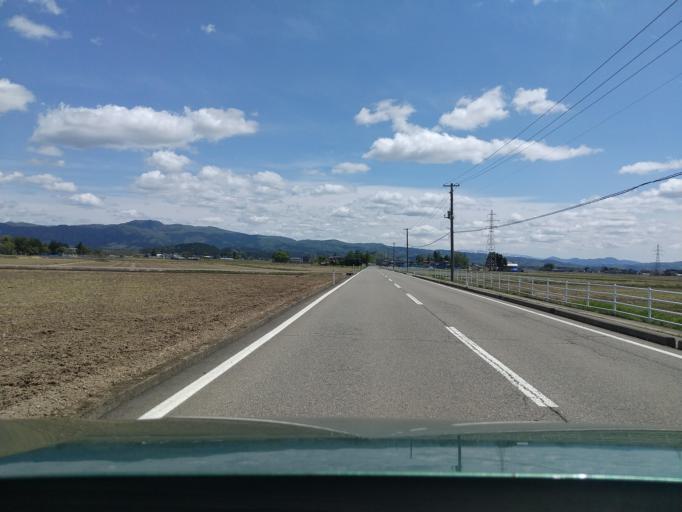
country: JP
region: Akita
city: Omagari
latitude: 39.3863
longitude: 140.5116
